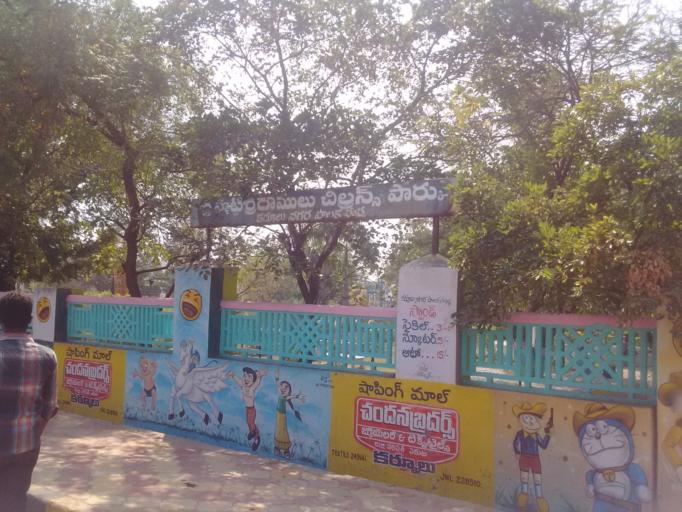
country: IN
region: Telangana
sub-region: Mahbubnagar
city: Alampur
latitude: 15.8338
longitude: 78.0419
